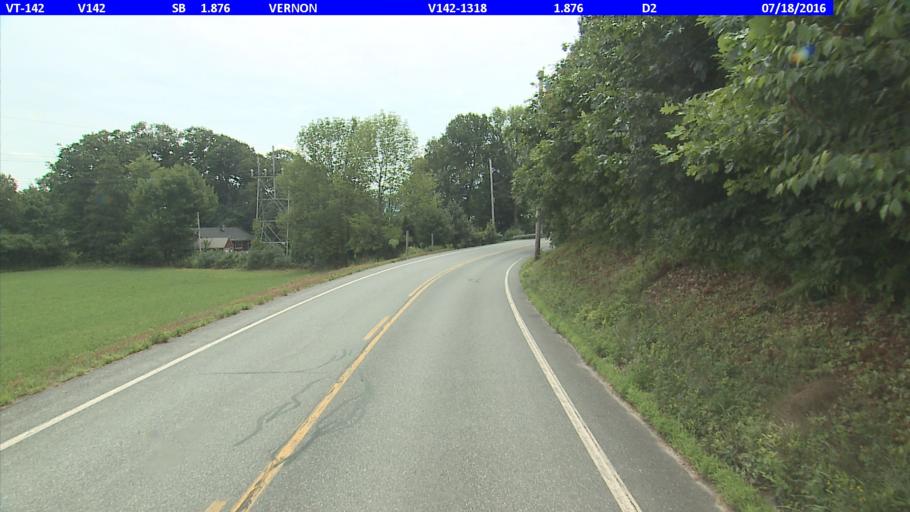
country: US
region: New Hampshire
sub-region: Cheshire County
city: Hinsdale
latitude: 42.7512
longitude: -72.4797
